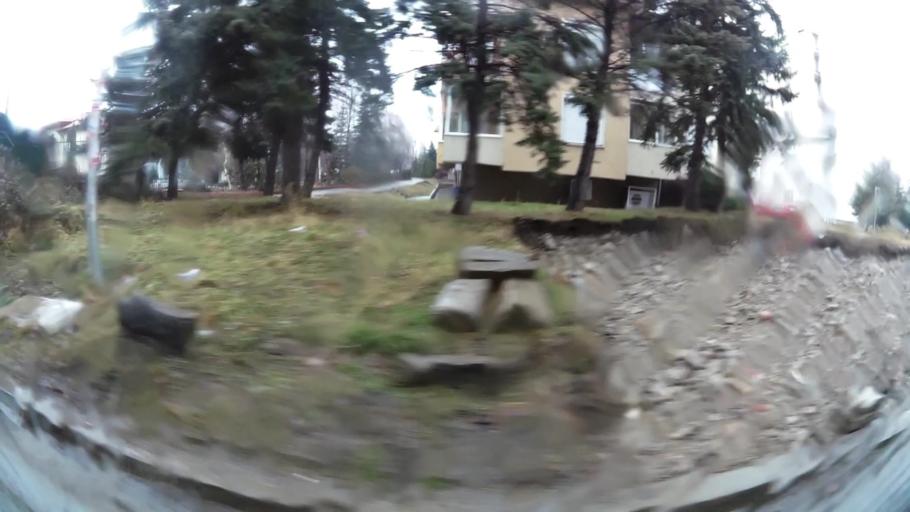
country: BG
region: Sofia-Capital
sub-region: Stolichna Obshtina
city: Sofia
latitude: 42.6478
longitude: 23.3381
